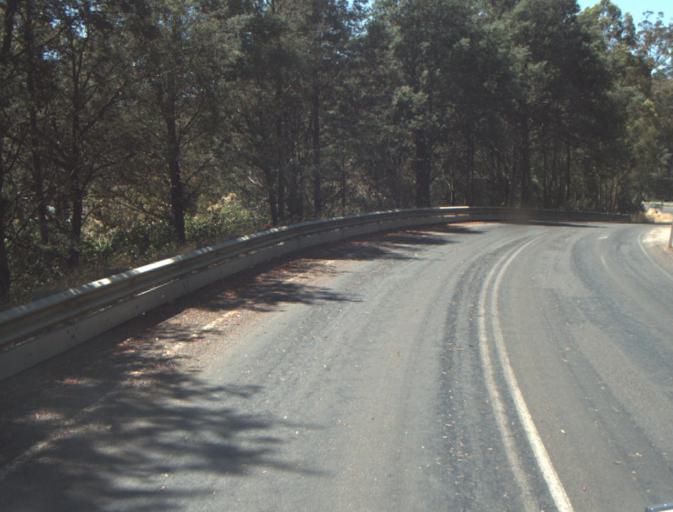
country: AU
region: Tasmania
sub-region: Launceston
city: Newstead
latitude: -41.3245
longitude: 147.3582
